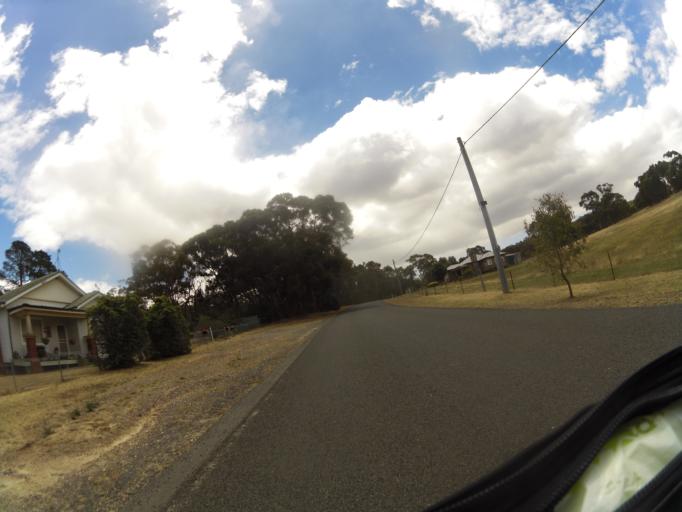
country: AU
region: Victoria
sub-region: Mount Alexander
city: Castlemaine
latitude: -37.0244
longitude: 144.2415
